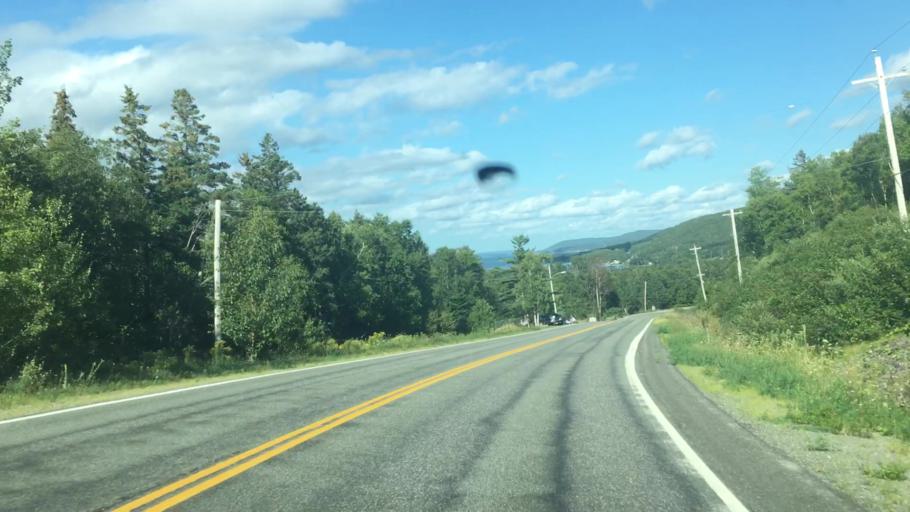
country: CA
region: Nova Scotia
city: Sydney
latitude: 45.8660
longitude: -60.6216
